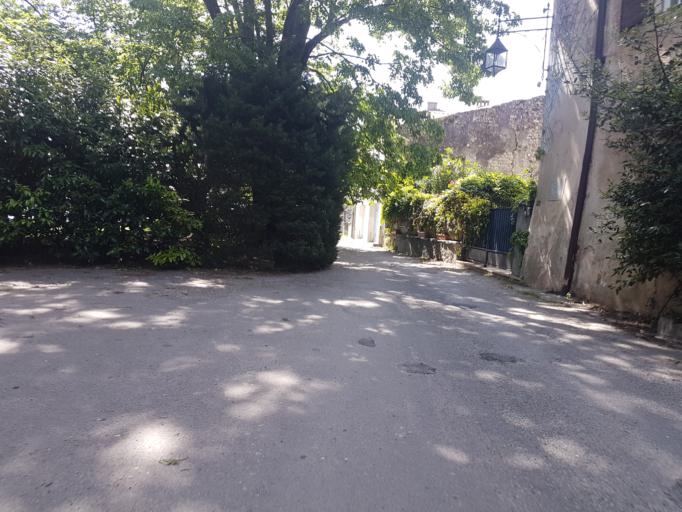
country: FR
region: Rhone-Alpes
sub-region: Departement de la Drome
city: Saulce-sur-Rhone
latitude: 44.7131
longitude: 4.7637
